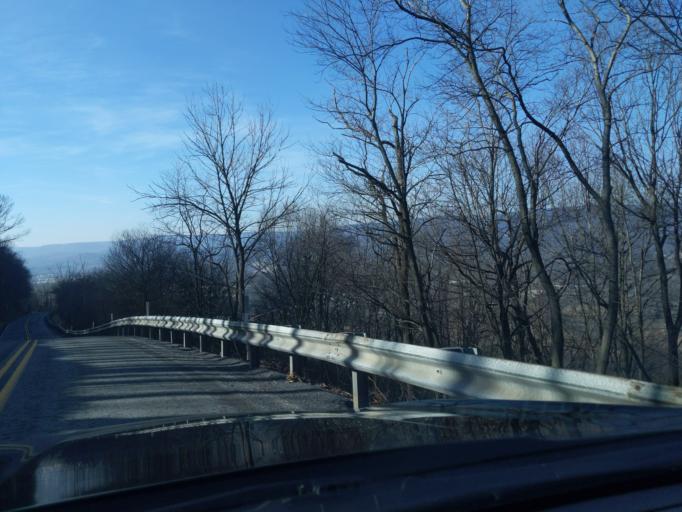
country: US
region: Pennsylvania
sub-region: Blair County
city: Tipton
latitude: 40.6213
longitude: -78.2822
